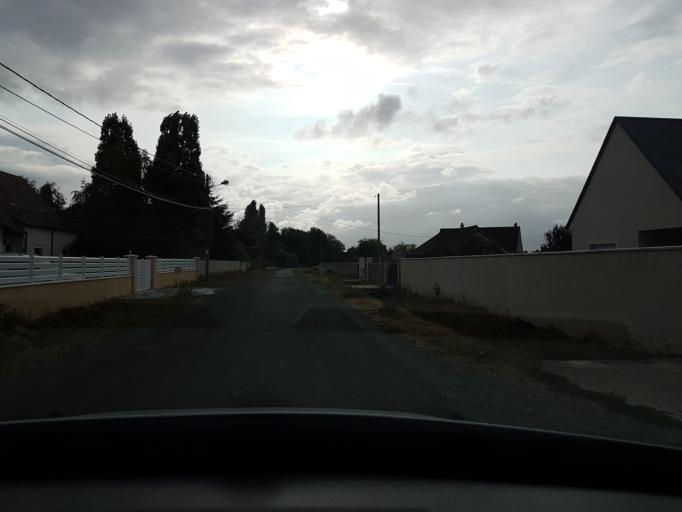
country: FR
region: Centre
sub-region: Departement d'Indre-et-Loire
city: Veretz
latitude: 47.3365
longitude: 0.8070
